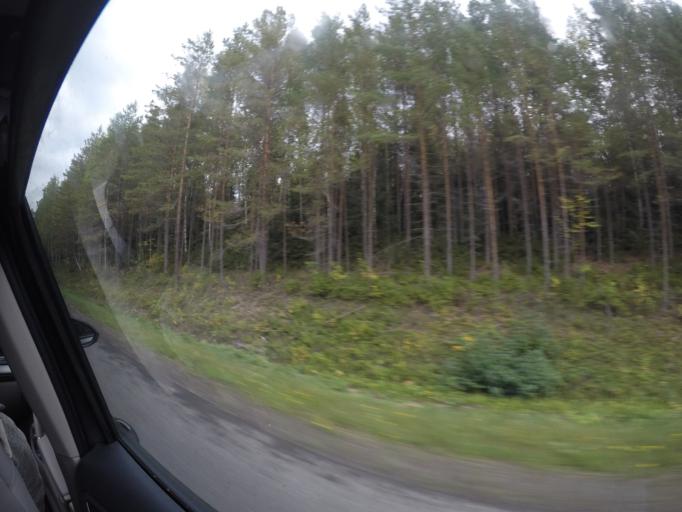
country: FI
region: Haeme
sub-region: Haemeenlinna
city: Parola
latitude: 61.1686
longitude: 24.4111
